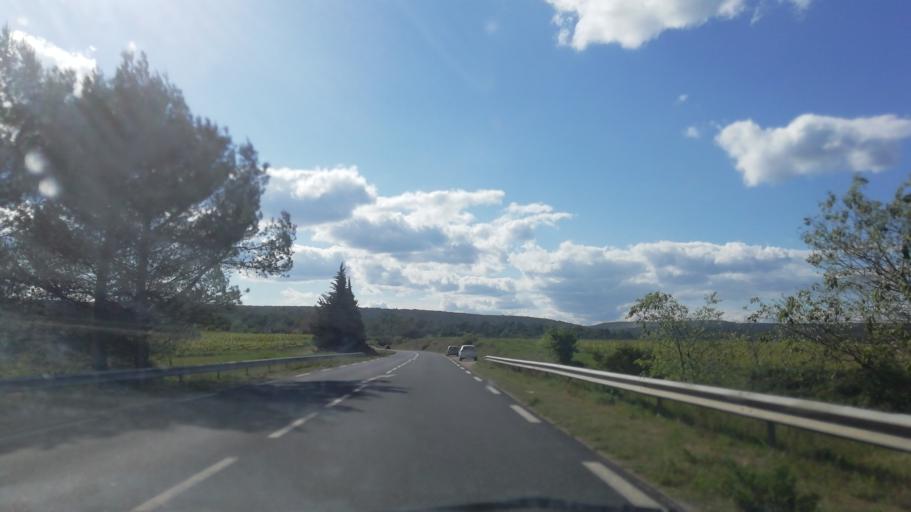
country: FR
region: Languedoc-Roussillon
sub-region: Departement de l'Herault
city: Saint-Gely-du-Fesc
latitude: 43.7082
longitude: 3.8092
